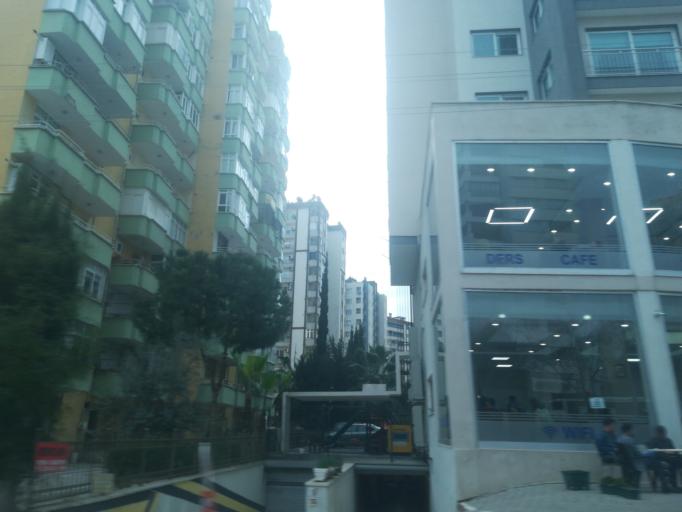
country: TR
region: Adana
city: Adana
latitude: 37.0459
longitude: 35.2901
